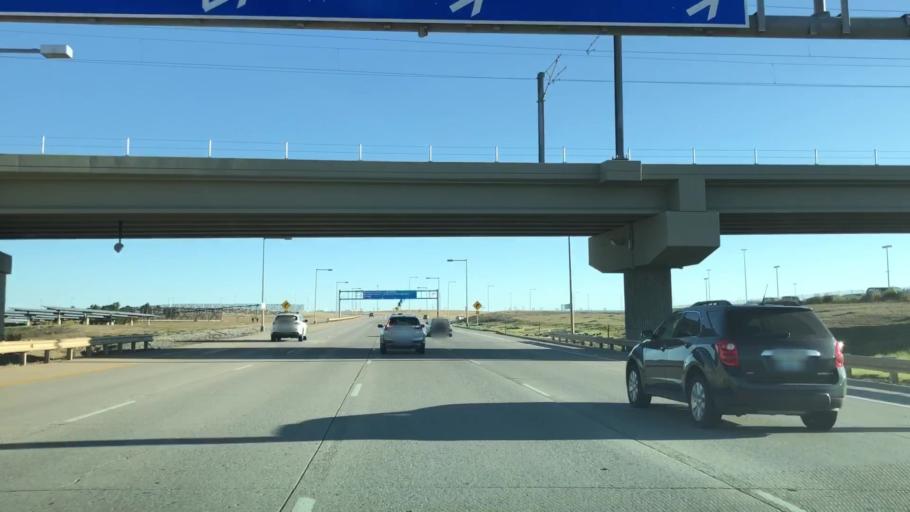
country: US
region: Colorado
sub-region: Weld County
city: Lochbuie
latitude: 39.8386
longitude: -104.6761
